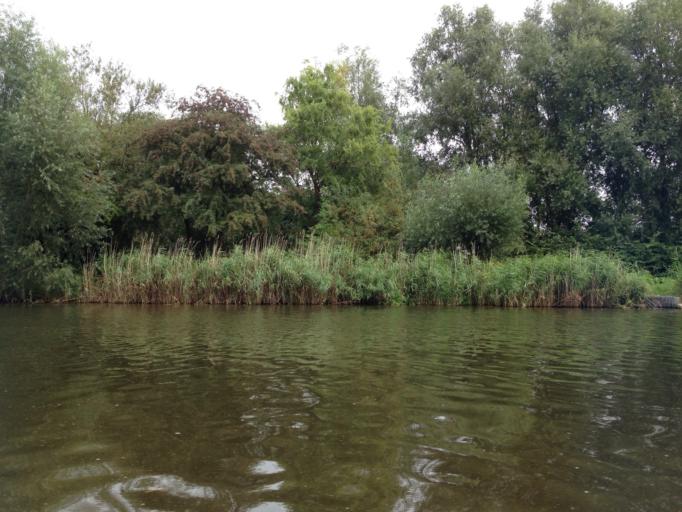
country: NL
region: South Holland
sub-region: Gemeente Vlaardingen
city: Vlaardingen
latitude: 51.9266
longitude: 4.3389
